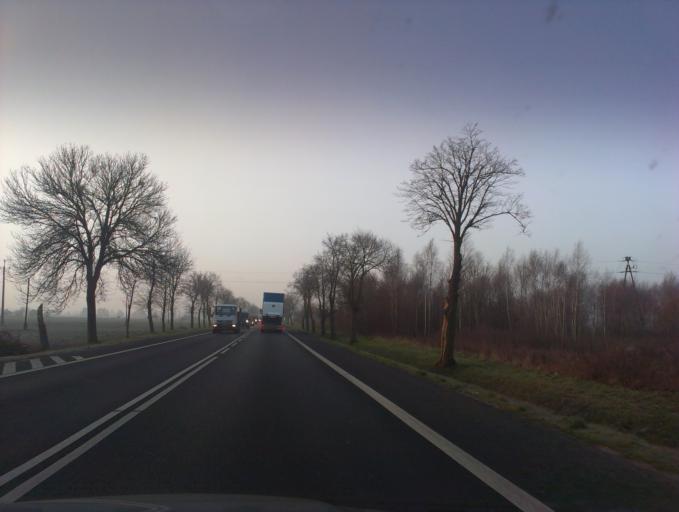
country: PL
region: Greater Poland Voivodeship
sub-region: Powiat obornicki
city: Rogozno
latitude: 52.7574
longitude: 16.9631
